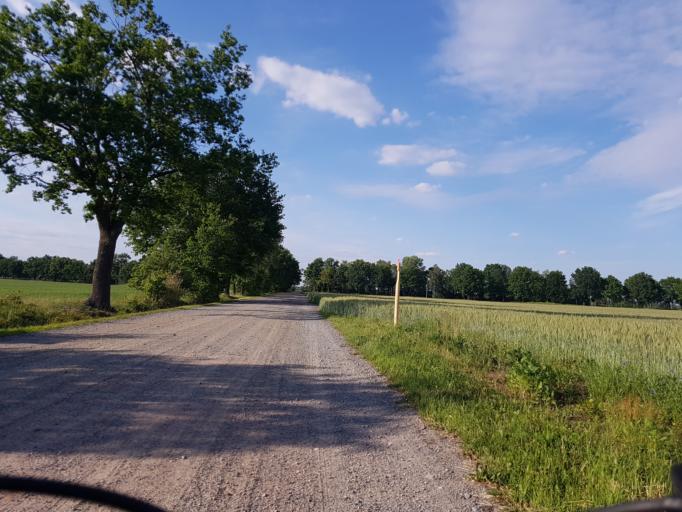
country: DE
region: Brandenburg
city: Elsterwerda
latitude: 51.4356
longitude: 13.5312
